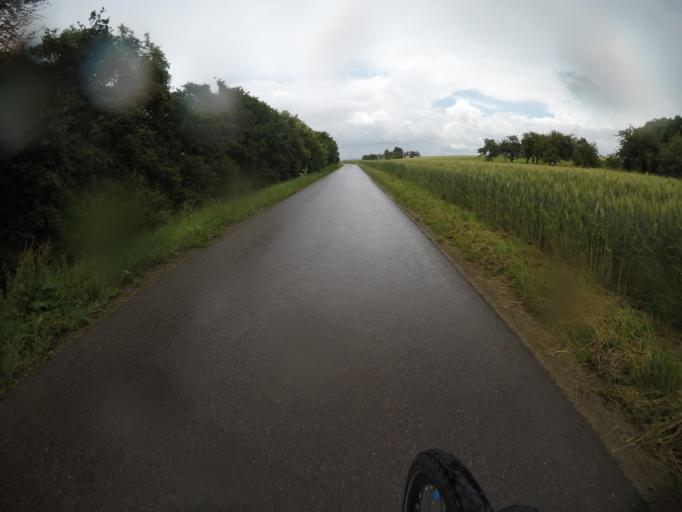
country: DE
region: Baden-Wuerttemberg
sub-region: Regierungsbezirk Stuttgart
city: Motzingen
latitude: 48.5119
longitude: 8.7920
